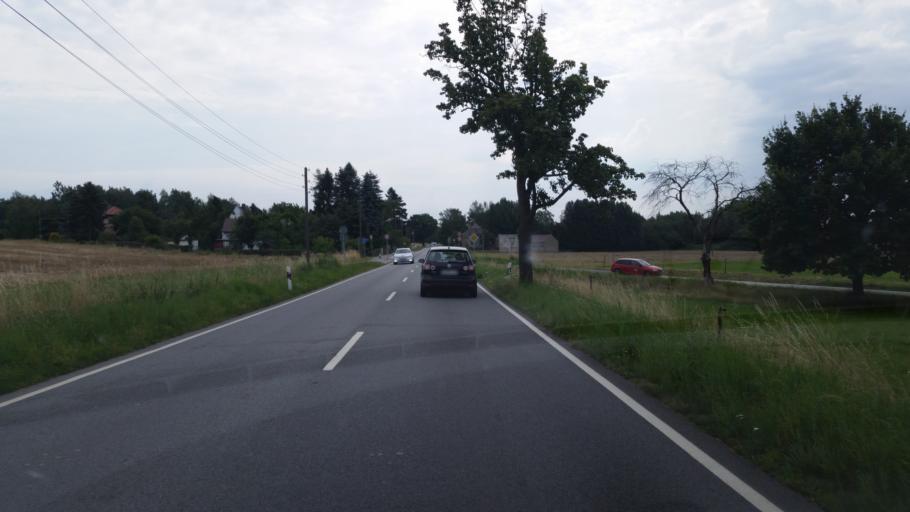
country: DE
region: Saxony
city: Kamenz
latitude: 51.2586
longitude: 14.1244
